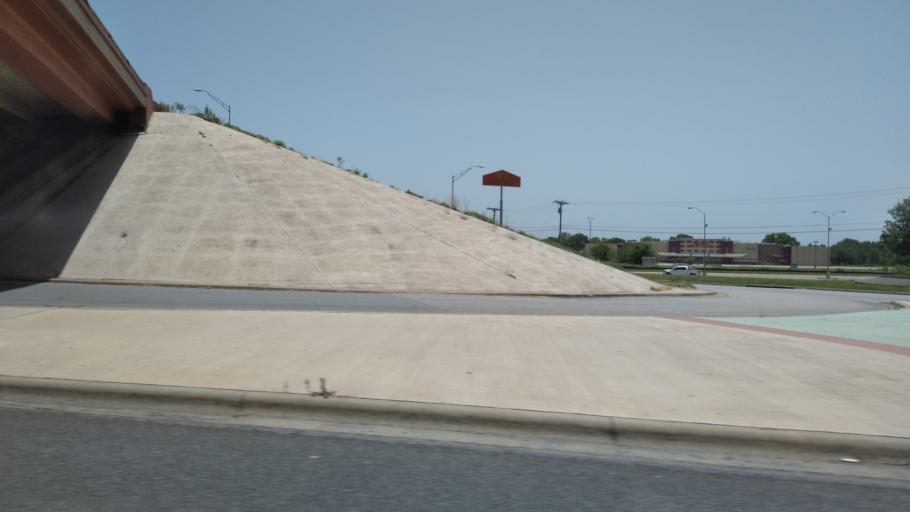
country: US
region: Texas
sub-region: McLennan County
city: Beverly Hills
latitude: 31.5275
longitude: -97.1627
